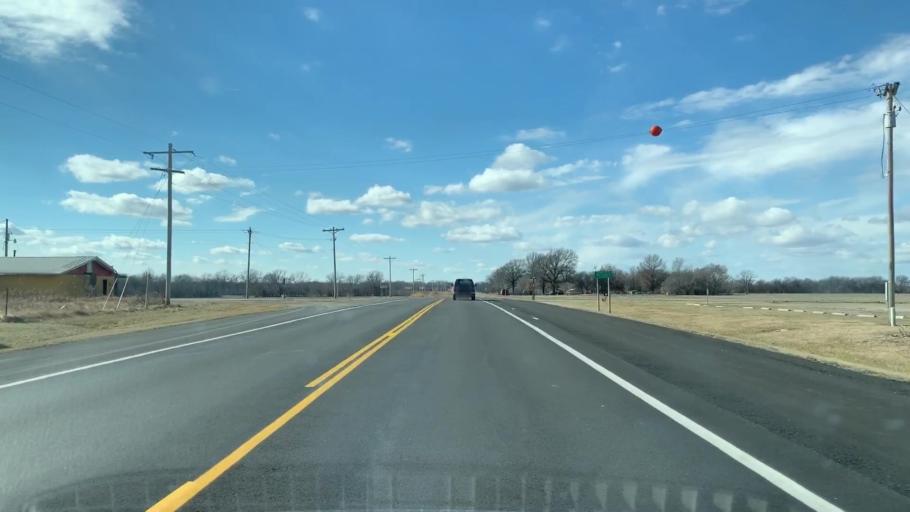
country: US
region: Kansas
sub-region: Labette County
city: Parsons
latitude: 37.3404
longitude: -95.1258
